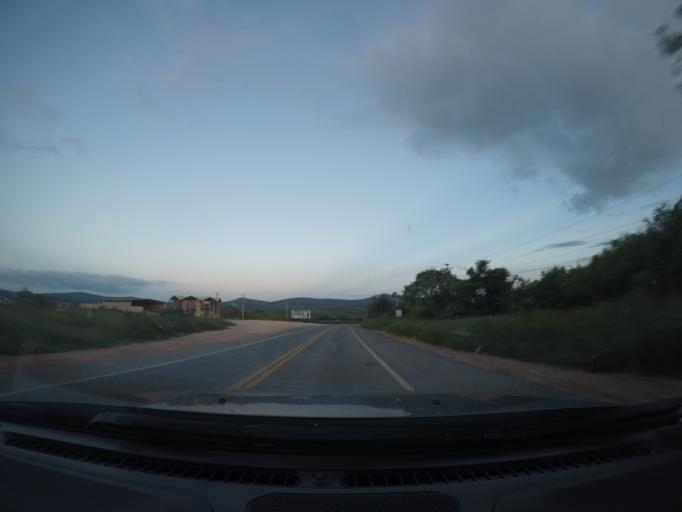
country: BR
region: Bahia
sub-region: Seabra
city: Seabra
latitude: -12.4266
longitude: -41.7651
